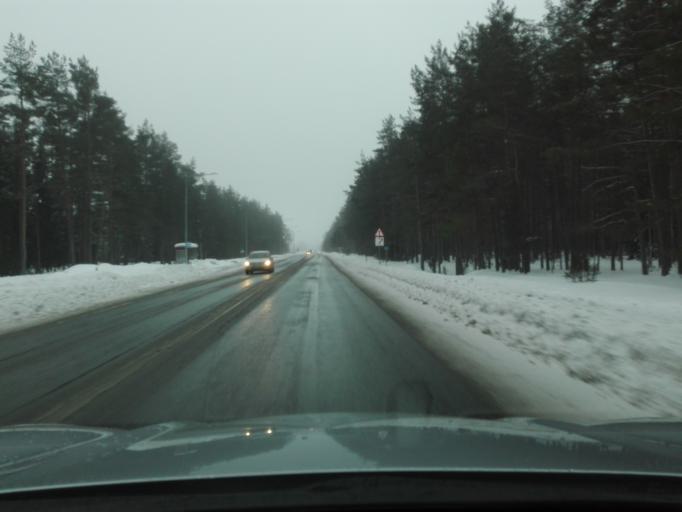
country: EE
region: Harju
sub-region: Kiili vald
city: Kiili
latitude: 59.3478
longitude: 24.7742
